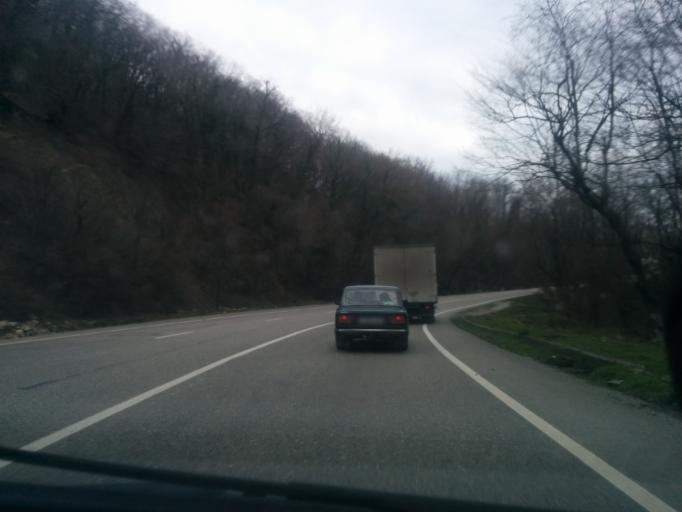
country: RU
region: Krasnodarskiy
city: Nebug
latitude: 44.1772
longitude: 38.9607
